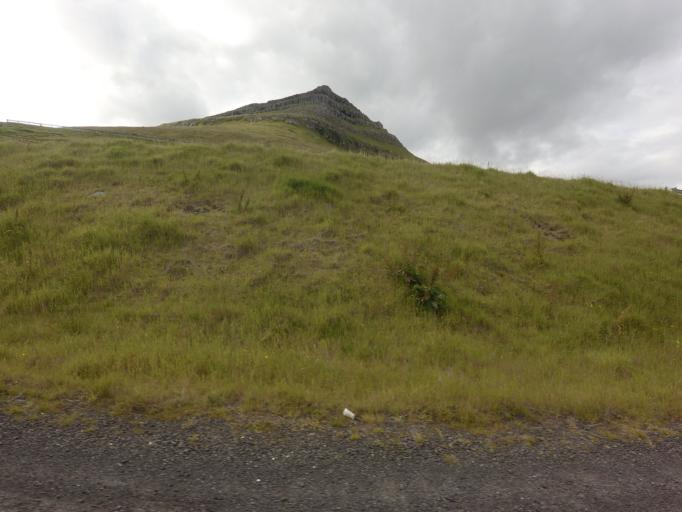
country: FO
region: Eysturoy
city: Eystur
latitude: 62.2085
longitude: -6.6910
